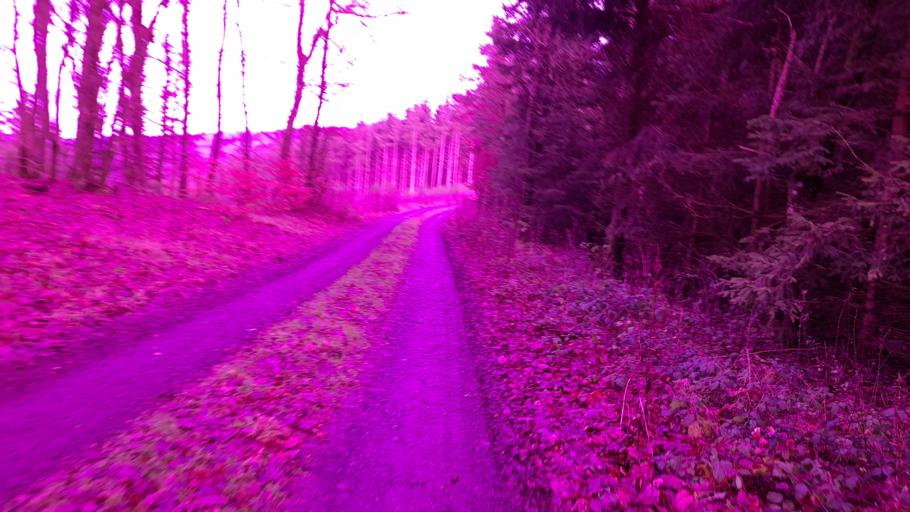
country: DE
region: Rheinland-Pfalz
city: Dasburg
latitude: 50.0804
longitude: 6.1060
